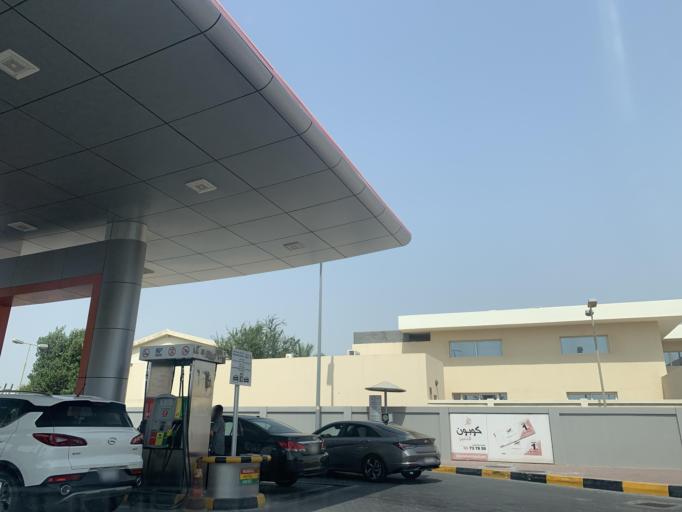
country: BH
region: Central Governorate
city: Madinat Hamad
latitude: 26.1670
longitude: 50.4656
